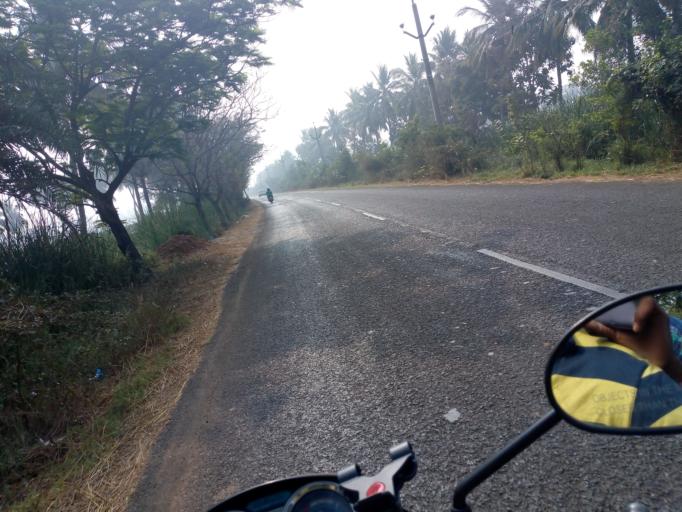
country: IN
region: Andhra Pradesh
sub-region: West Godavari
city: Tadepallegudem
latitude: 16.7953
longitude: 81.4158
